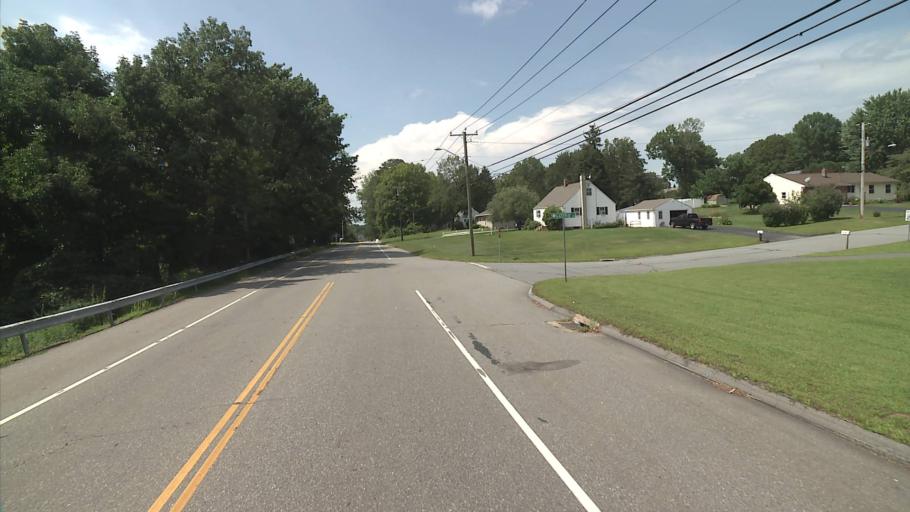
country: US
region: Connecticut
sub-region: New London County
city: Colchester
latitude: 41.5634
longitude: -72.3178
